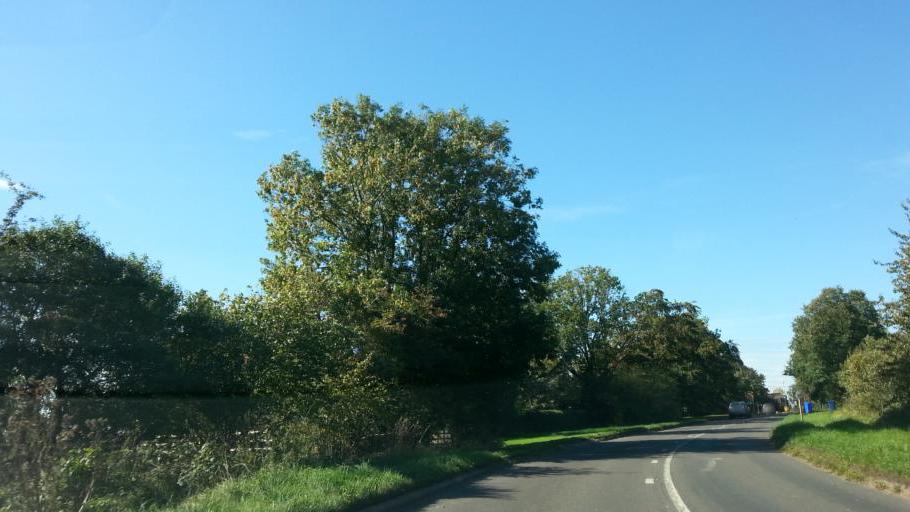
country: GB
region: England
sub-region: Staffordshire
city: Gnosall
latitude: 52.7841
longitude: -2.2447
